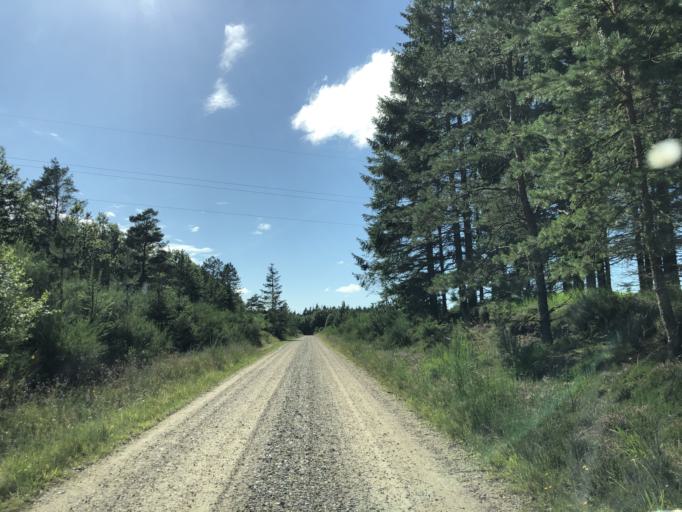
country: DK
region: Central Jutland
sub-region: Holstebro Kommune
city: Ulfborg
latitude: 56.2187
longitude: 8.4622
